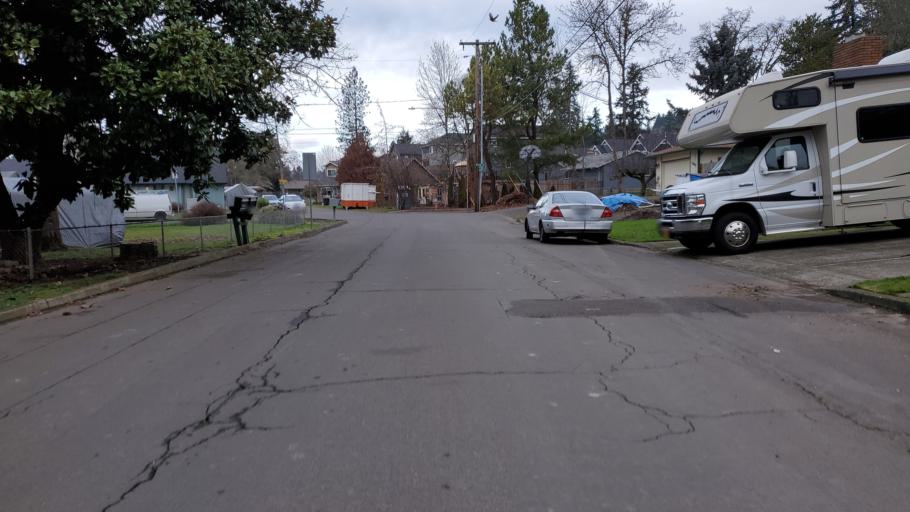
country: US
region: Oregon
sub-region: Clackamas County
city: Gladstone
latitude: 45.3885
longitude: -122.5966
